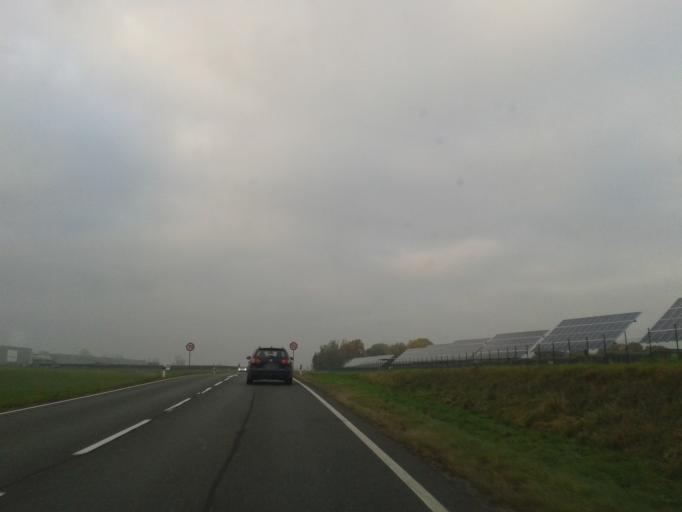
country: DE
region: Saxony
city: Niederschona
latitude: 50.9290
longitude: 13.4017
